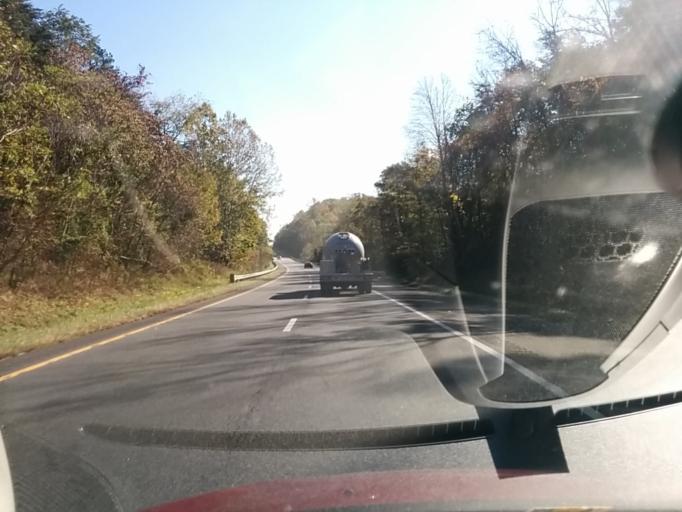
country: US
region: Virginia
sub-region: Albemarle County
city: Crozet
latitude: 38.0302
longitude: -78.6755
